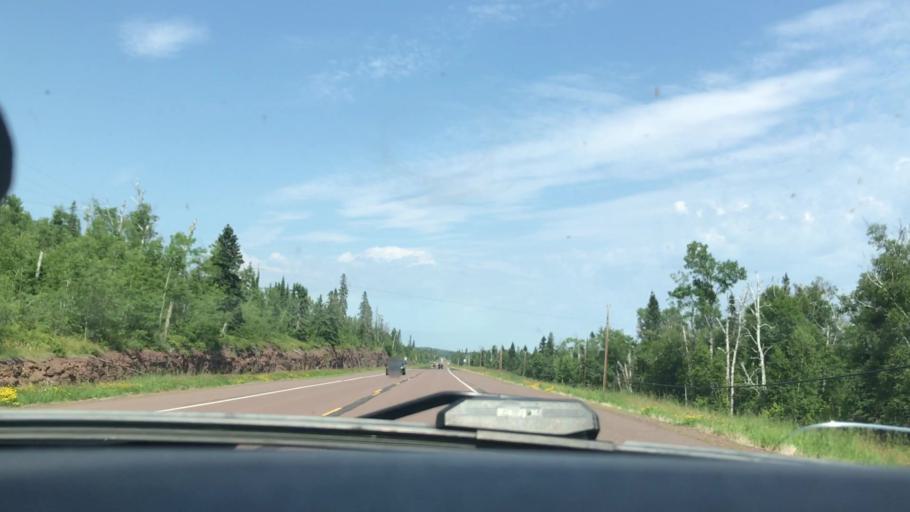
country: US
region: Minnesota
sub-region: Cook County
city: Grand Marais
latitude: 47.6233
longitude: -90.7428
